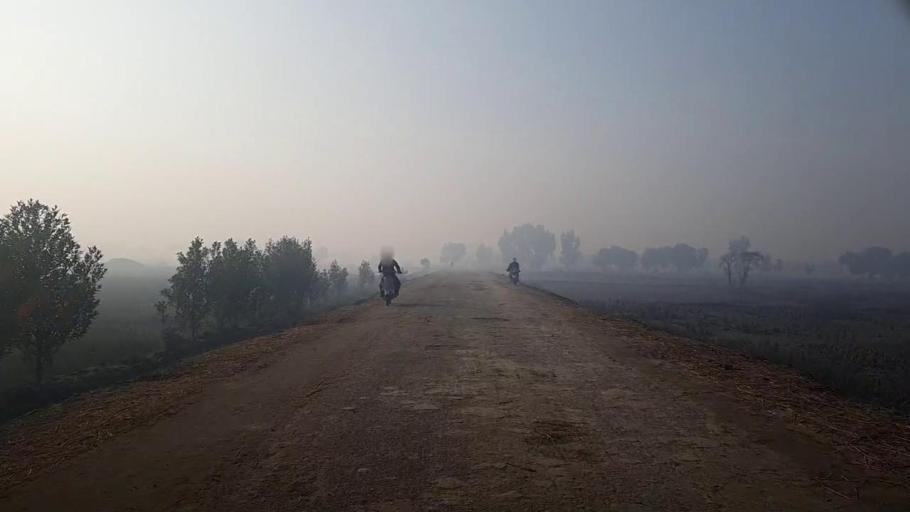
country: PK
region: Sindh
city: Mehar
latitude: 27.1549
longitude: 67.8239
